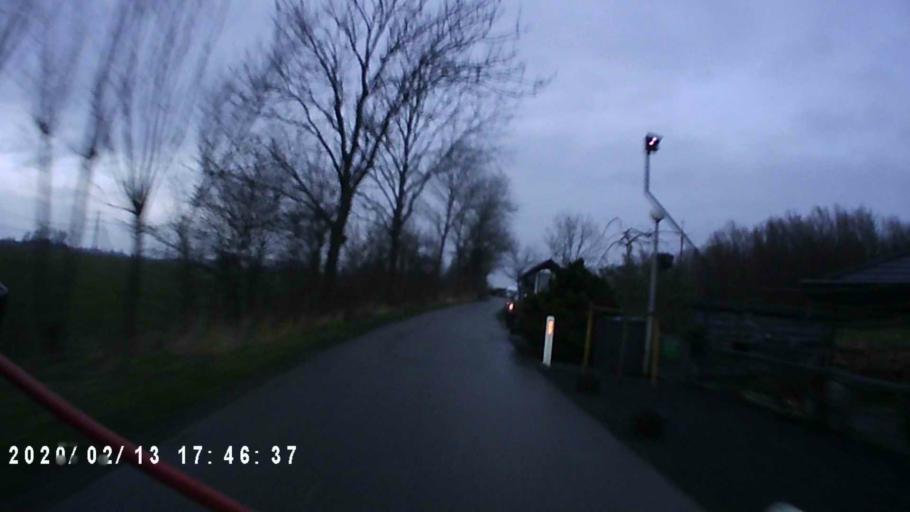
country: NL
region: Groningen
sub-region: Gemeente Zuidhorn
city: Aduard
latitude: 53.2318
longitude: 6.4736
